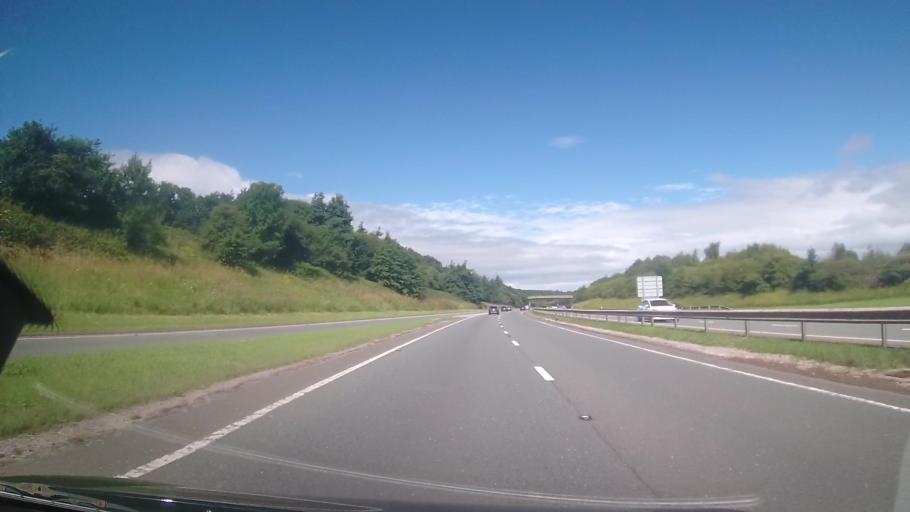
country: GB
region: Wales
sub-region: County of Flintshire
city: Flint
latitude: 53.2134
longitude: -3.1341
